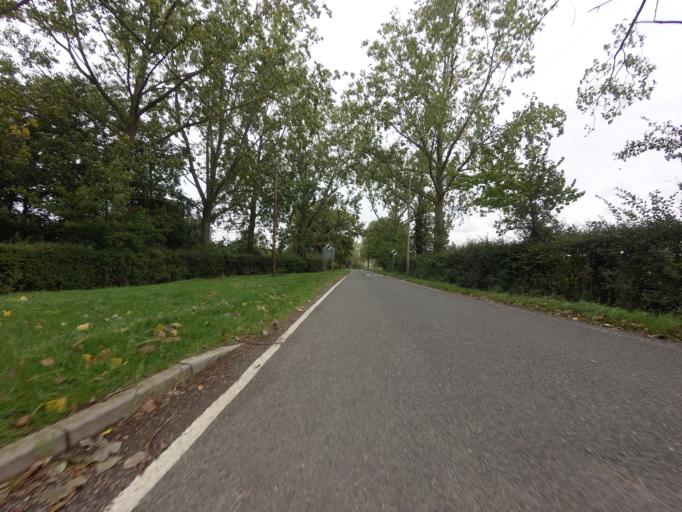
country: GB
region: England
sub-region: Cambridgeshire
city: Duxford
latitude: 51.9980
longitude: 0.1085
